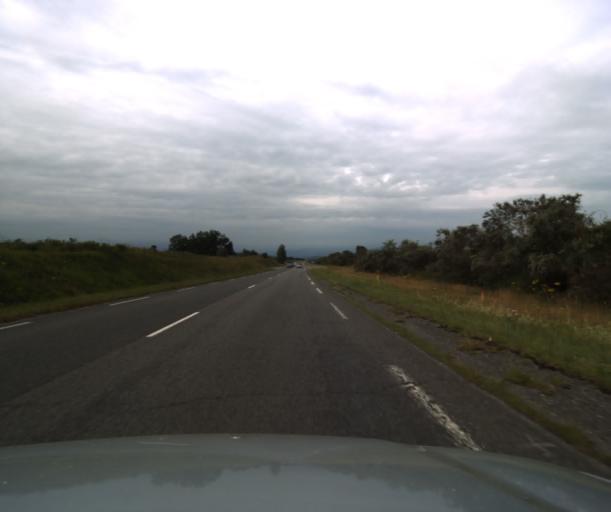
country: FR
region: Midi-Pyrenees
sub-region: Departement des Hautes-Pyrenees
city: Juillan
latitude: 43.2066
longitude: 0.0106
